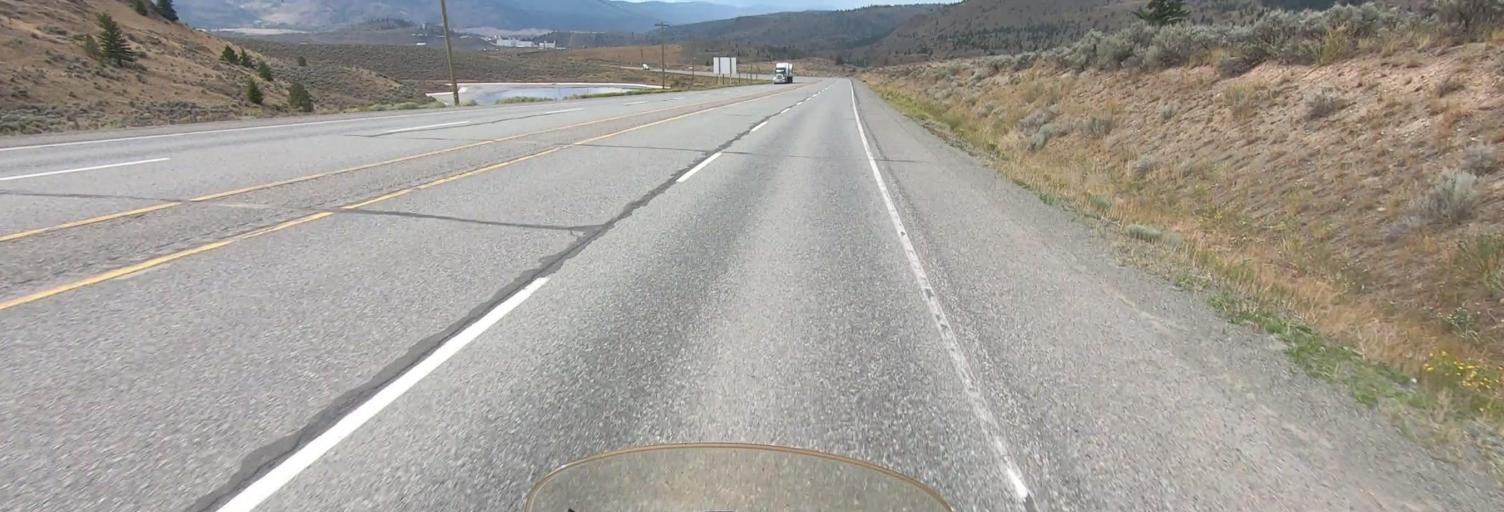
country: CA
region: British Columbia
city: Kamloops
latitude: 50.6701
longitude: -120.4764
